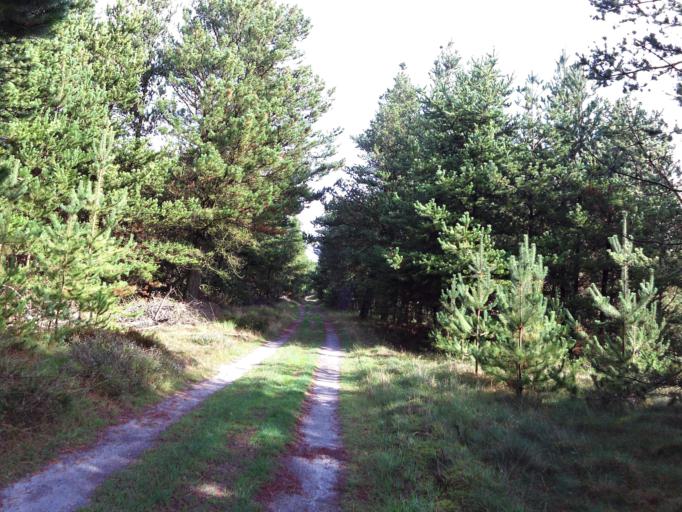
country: DK
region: South Denmark
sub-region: Varde Kommune
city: Oksbol
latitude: 55.5523
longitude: 8.2087
